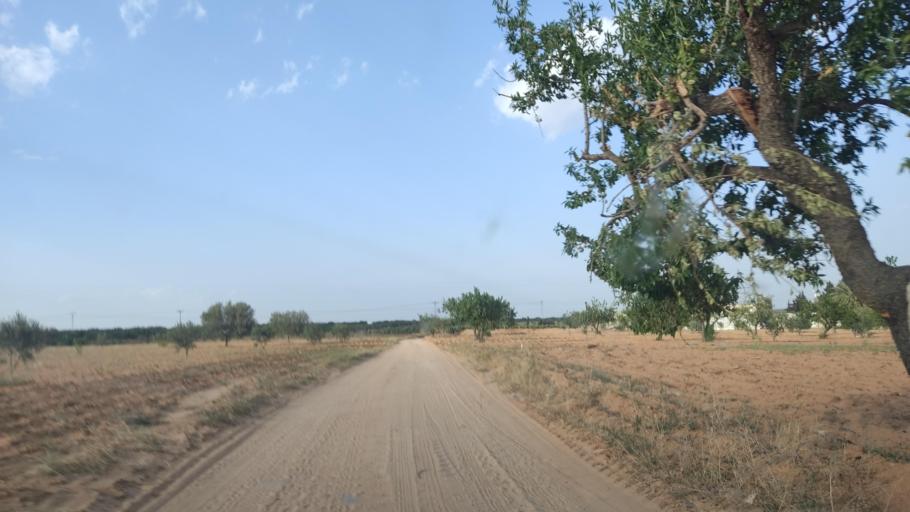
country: TN
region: Safaqis
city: Sfax
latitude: 34.8579
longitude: 10.5997
